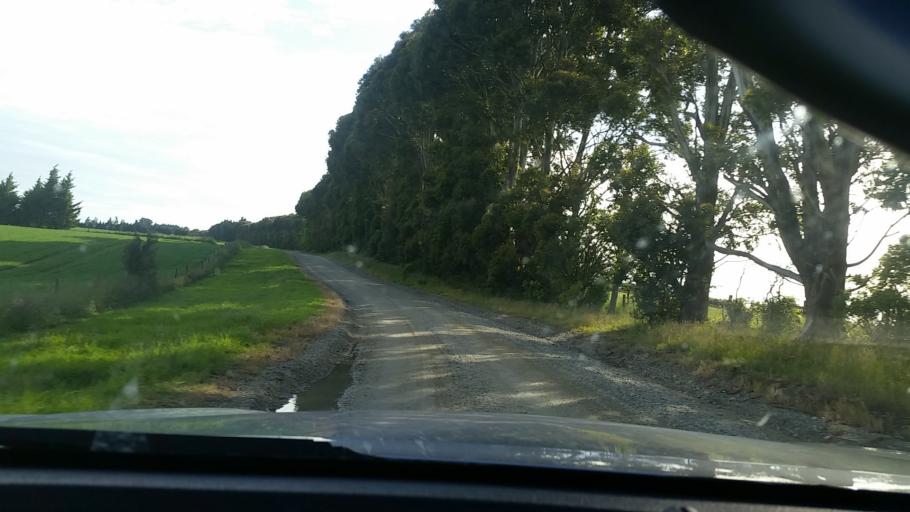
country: NZ
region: Southland
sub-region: Gore District
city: Gore
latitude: -46.2632
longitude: 168.7339
